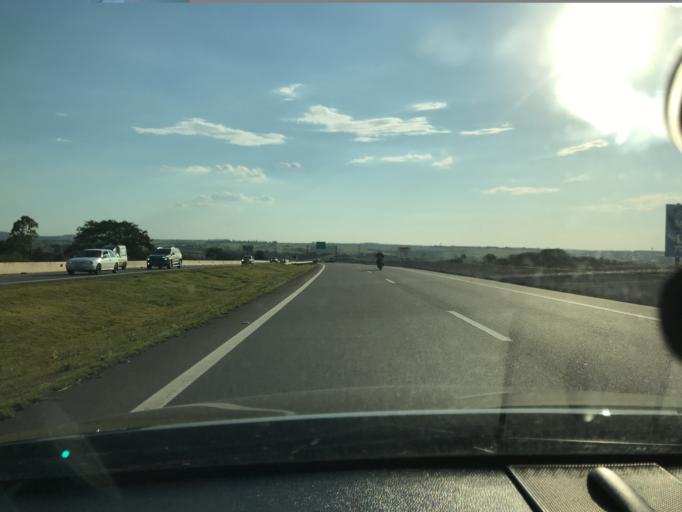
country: BR
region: Sao Paulo
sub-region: Valinhos
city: Valinhos
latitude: -22.9935
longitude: -47.0720
